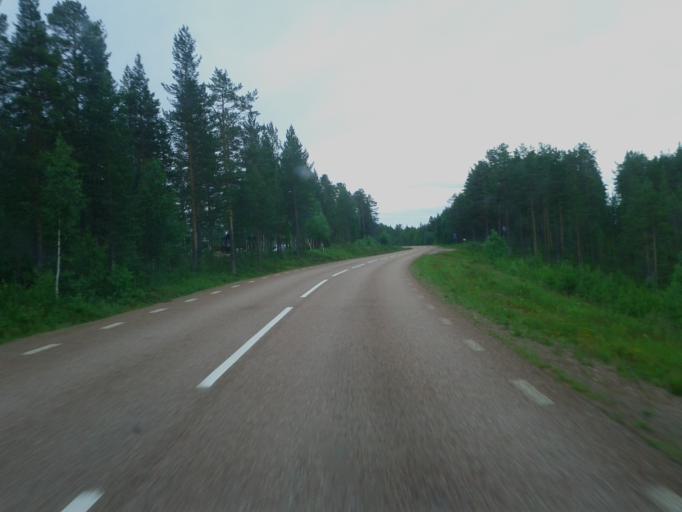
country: SE
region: Dalarna
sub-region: Alvdalens Kommun
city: AElvdalen
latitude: 61.5300
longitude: 13.3579
